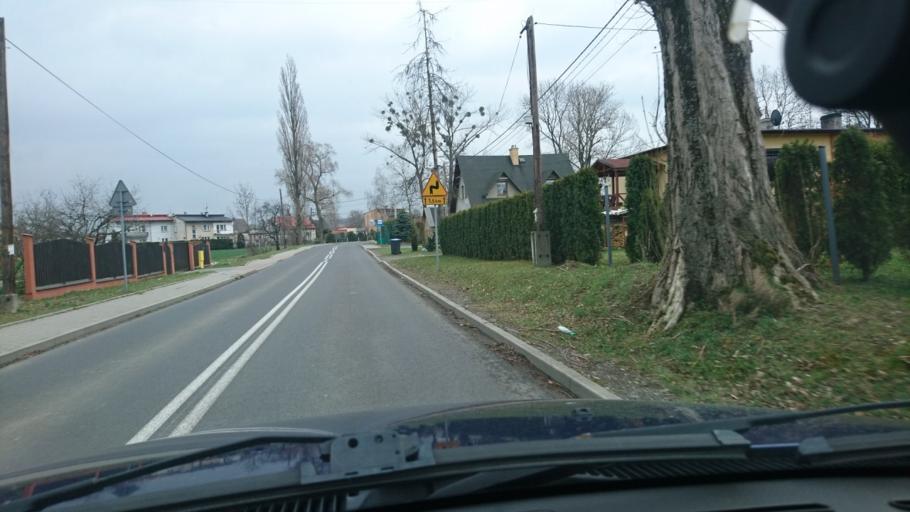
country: PL
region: Silesian Voivodeship
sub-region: Powiat bielski
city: Ligota
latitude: 49.8764
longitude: 18.9516
